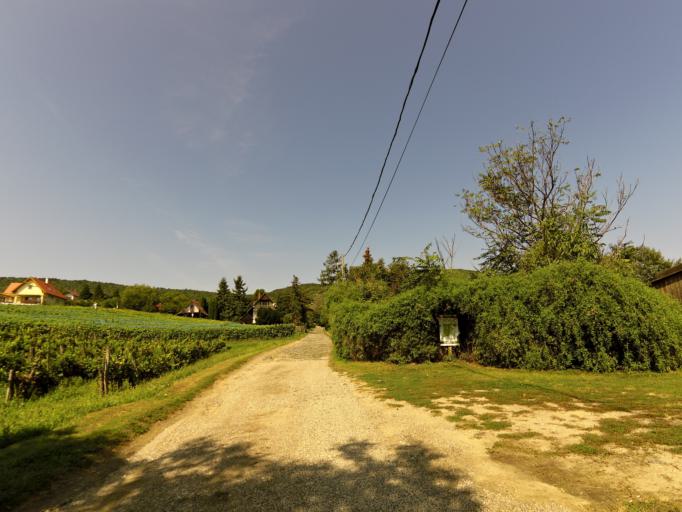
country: HU
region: Zala
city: Vonyarcvashegy
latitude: 46.7845
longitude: 17.3743
